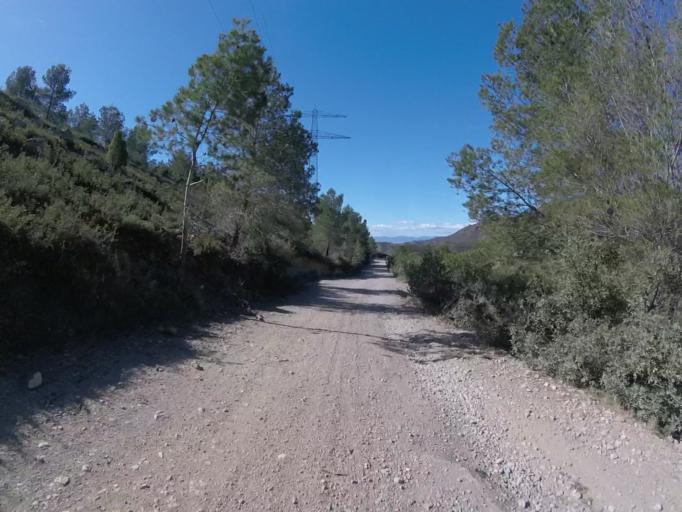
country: ES
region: Valencia
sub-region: Provincia de Castello
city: Benicassim
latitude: 40.0797
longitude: 0.0806
